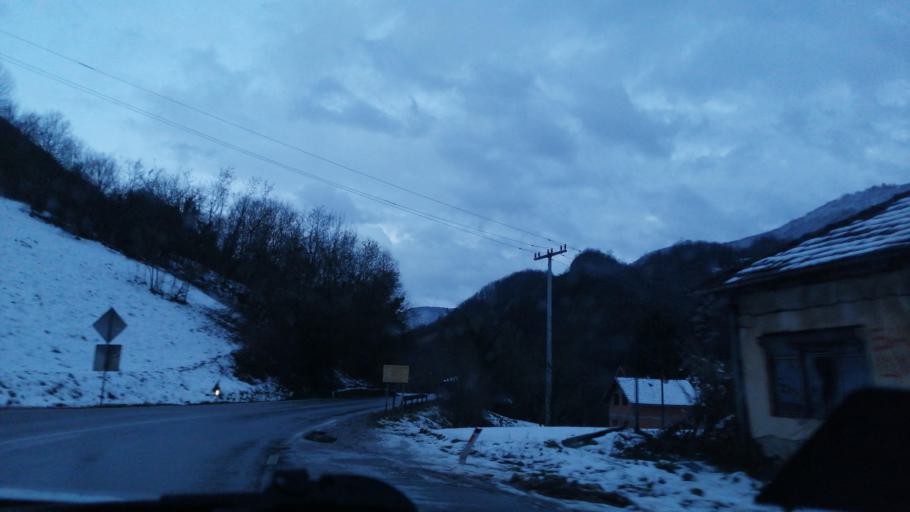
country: RS
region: Central Serbia
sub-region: Macvanski Okrug
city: Mali Zvornik
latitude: 44.2806
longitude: 19.1459
